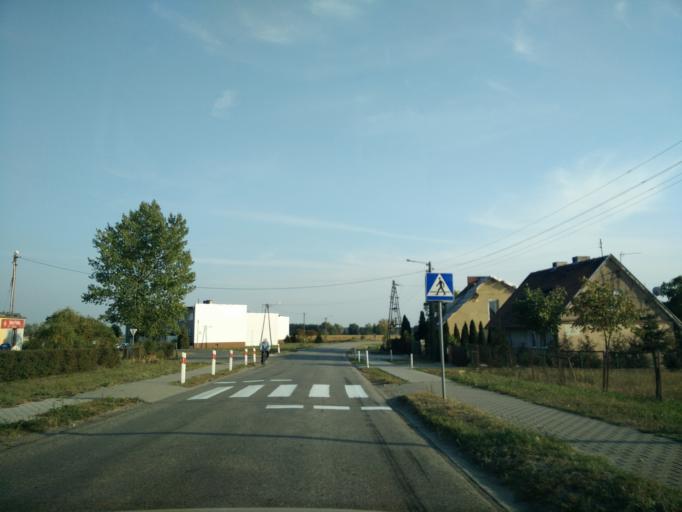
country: PL
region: Greater Poland Voivodeship
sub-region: Powiat sredzki
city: Sroda Wielkopolska
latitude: 52.1744
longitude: 17.2910
